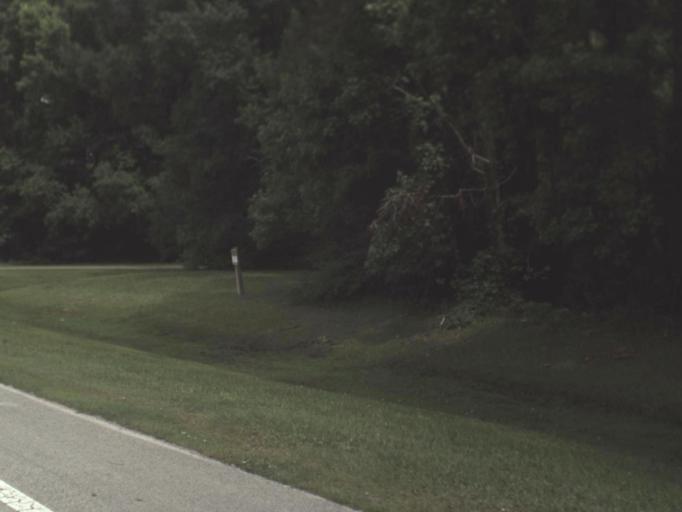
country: US
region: Florida
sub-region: Nassau County
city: Nassau Village-Ratliff
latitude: 30.4890
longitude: -81.6722
